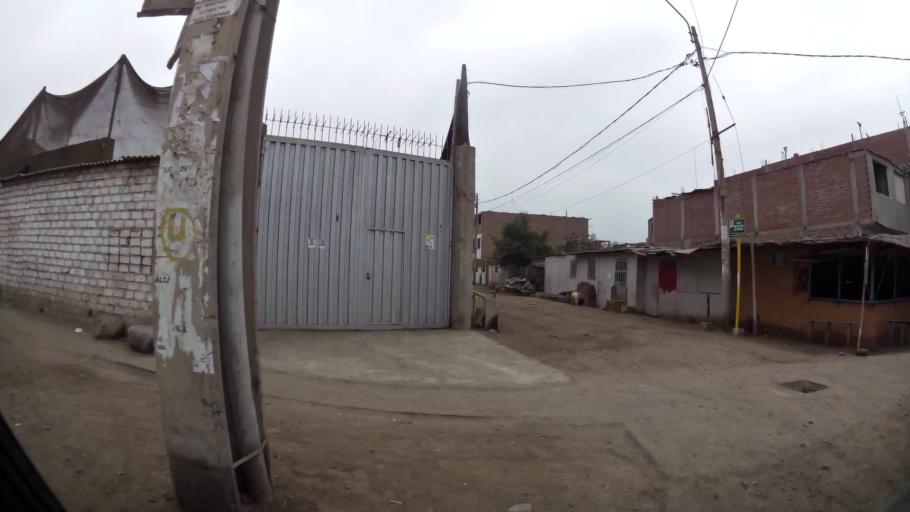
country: PE
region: Lima
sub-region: Lima
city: Urb. Santo Domingo
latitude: -11.8960
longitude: -77.0633
